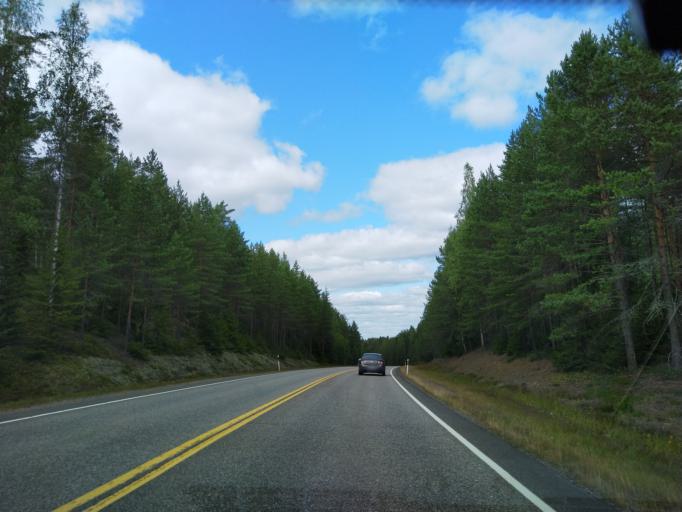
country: FI
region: Haeme
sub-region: Riihimaeki
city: Loppi
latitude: 60.7400
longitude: 24.3640
